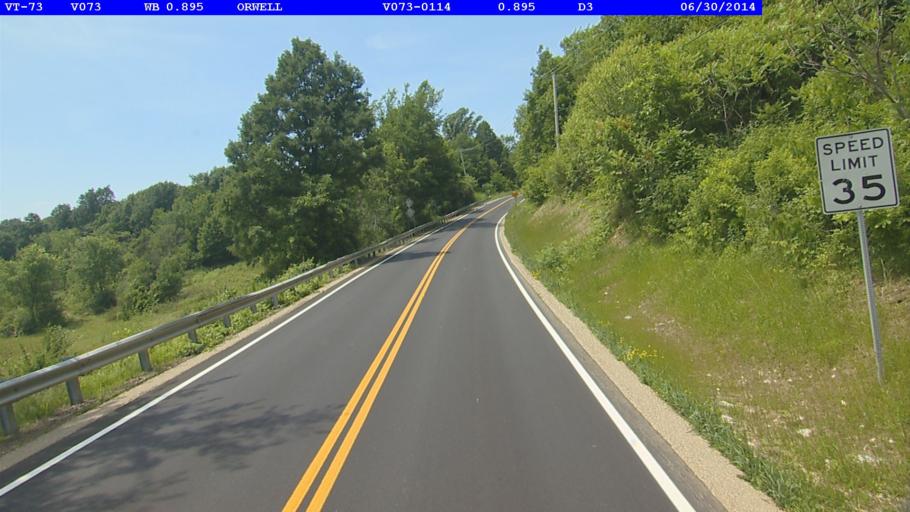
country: US
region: New York
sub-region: Essex County
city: Ticonderoga
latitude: 43.8022
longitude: -73.2881
